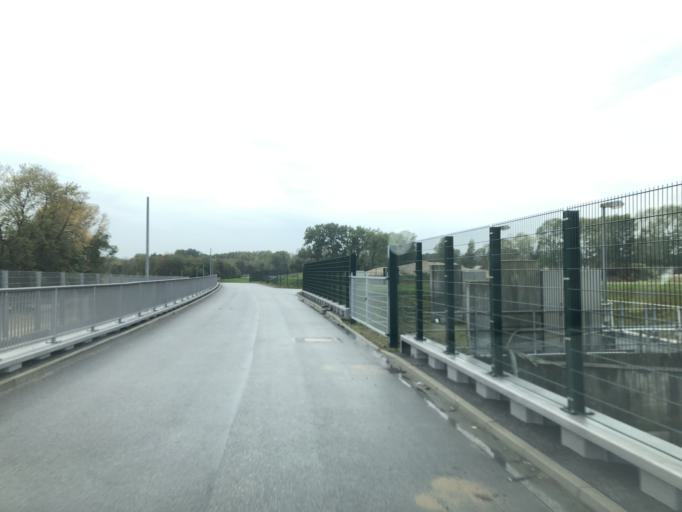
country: DE
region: Hamburg
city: Harburg
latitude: 53.4941
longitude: 9.9483
